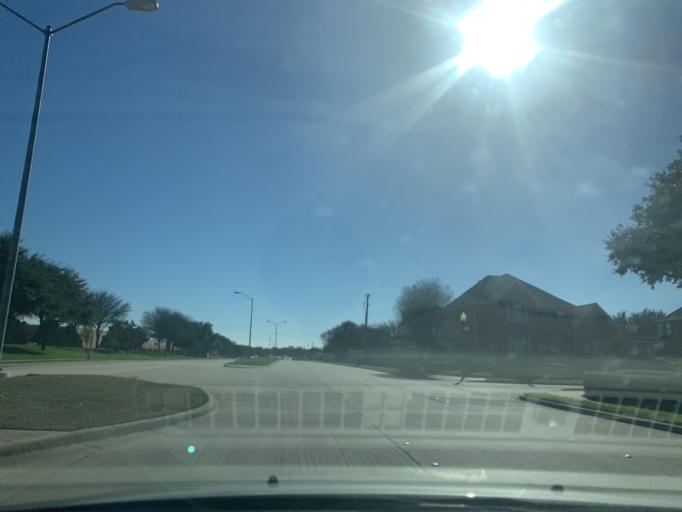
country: US
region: Texas
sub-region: Denton County
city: The Colony
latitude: 33.0480
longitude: -96.8332
